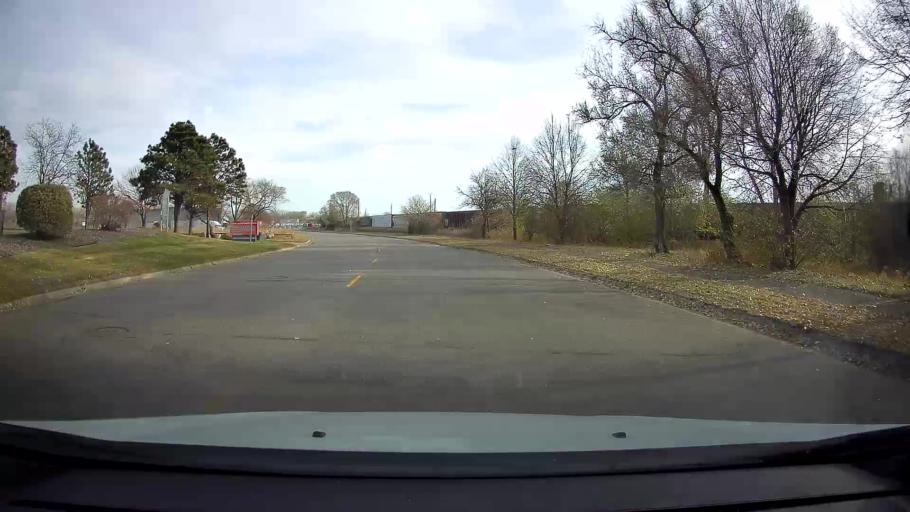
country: US
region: Minnesota
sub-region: Ramsey County
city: Lauderdale
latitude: 44.9790
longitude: -93.2123
